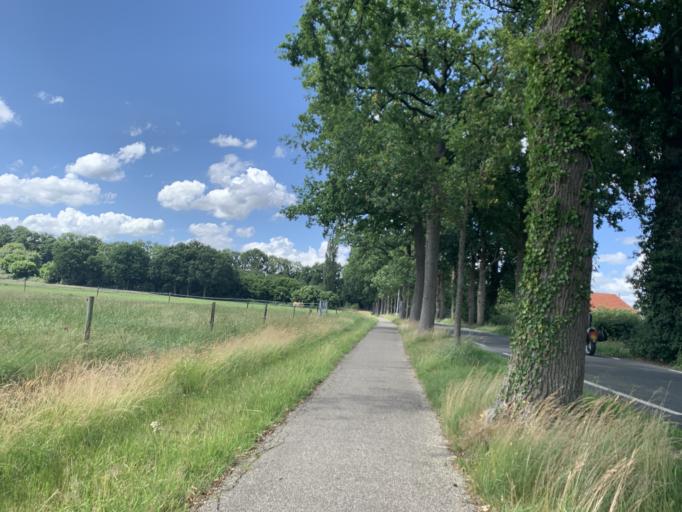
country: NL
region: Drenthe
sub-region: Gemeente Tynaarlo
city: Zuidlaren
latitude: 53.1350
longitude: 6.6555
